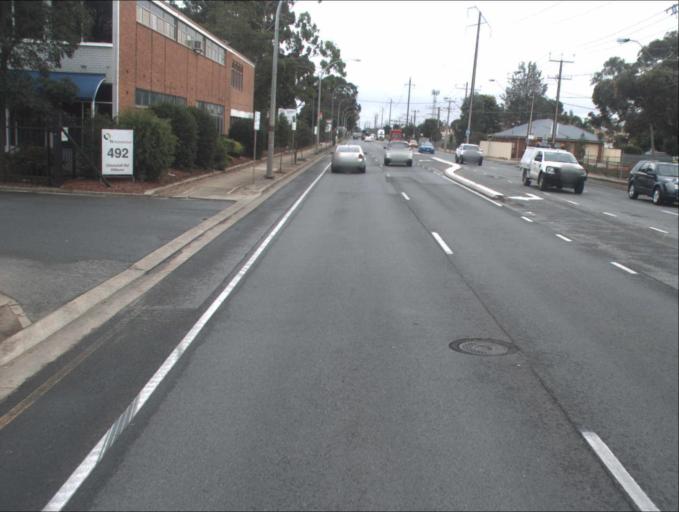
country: AU
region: South Australia
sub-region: Port Adelaide Enfield
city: Blair Athol
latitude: -34.8563
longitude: 138.5827
